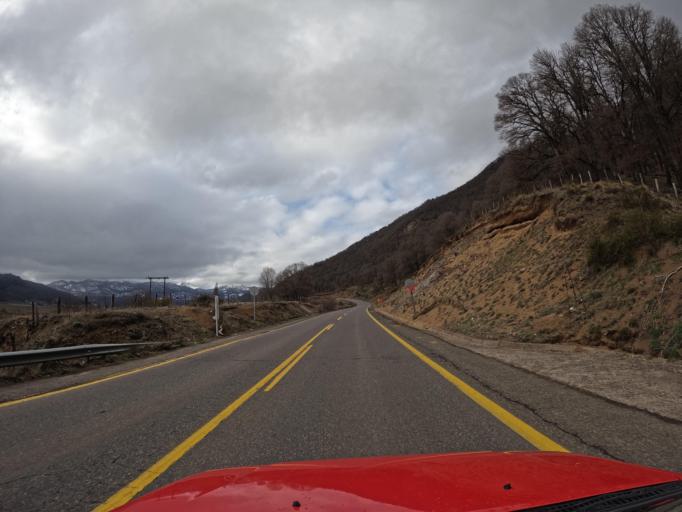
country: AR
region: Neuquen
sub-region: Departamento de Loncopue
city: Loncopue
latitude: -38.4805
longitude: -71.3645
